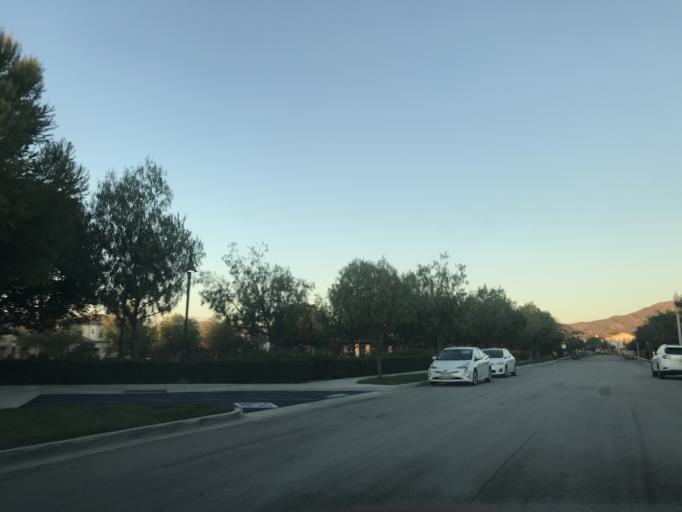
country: US
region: California
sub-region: Orange County
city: Lake Forest
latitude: 33.7042
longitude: -117.7383
